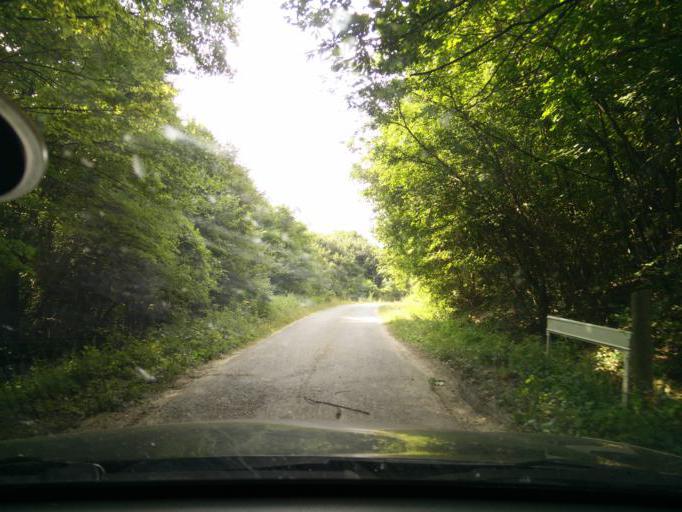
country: HU
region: Komarom-Esztergom
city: Sutto
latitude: 47.7120
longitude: 18.4583
